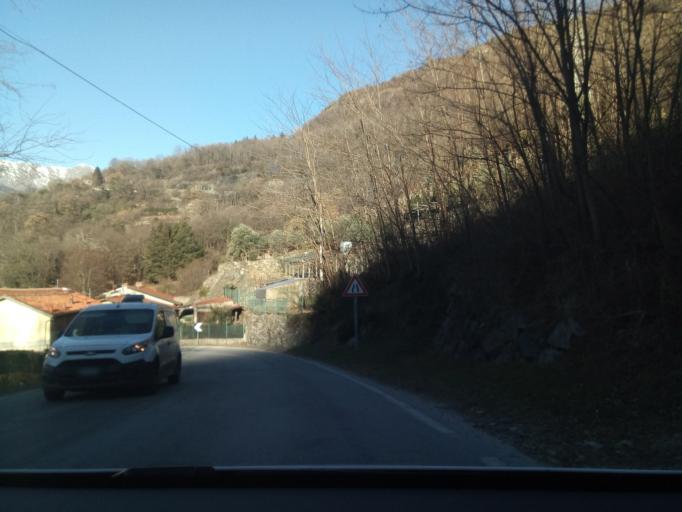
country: IT
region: Piedmont
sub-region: Provincia di Torino
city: Andrate
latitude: 45.5168
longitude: 7.8737
